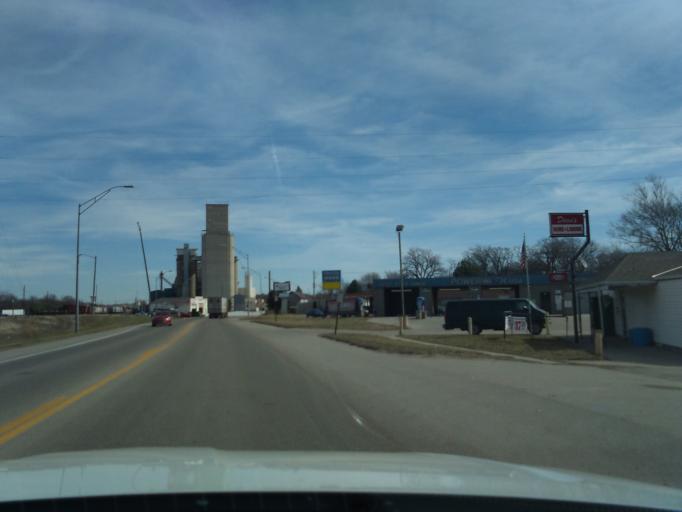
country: US
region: Nebraska
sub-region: Saline County
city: Crete
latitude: 40.6245
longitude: -96.9686
